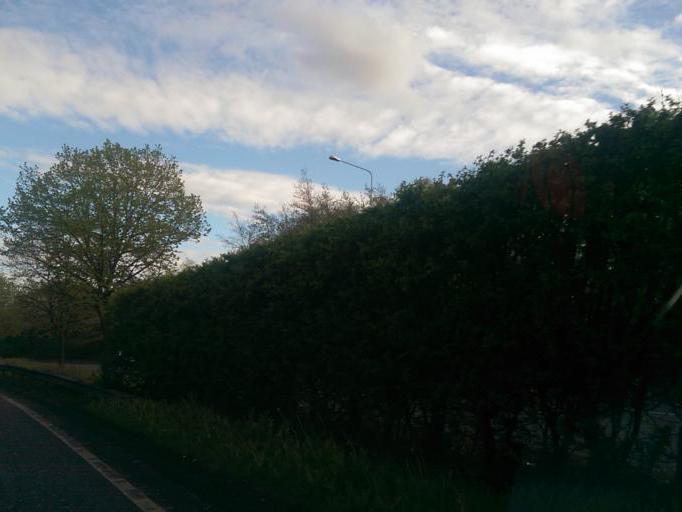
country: IE
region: Leinster
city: Ballyfermot
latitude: 53.3515
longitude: -6.3575
